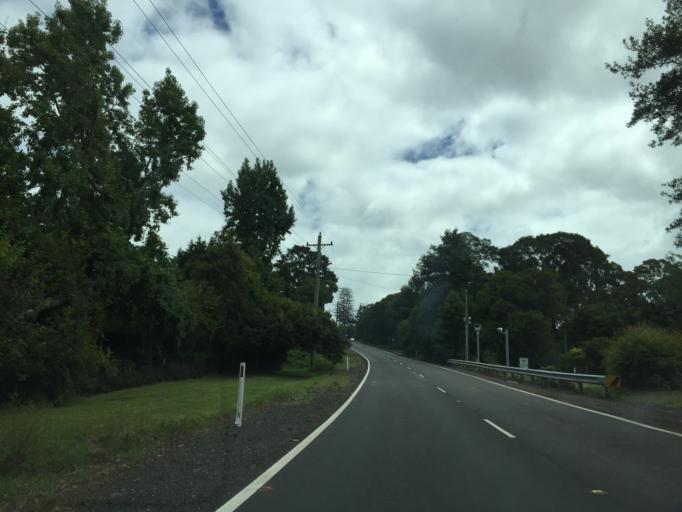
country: AU
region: New South Wales
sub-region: Hawkesbury
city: Richmond
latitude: -33.5341
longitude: 150.6327
